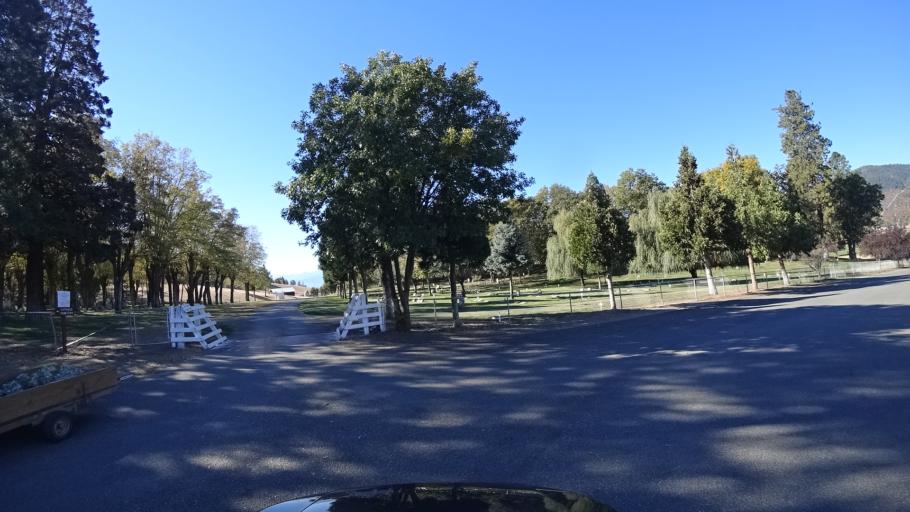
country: US
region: California
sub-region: Siskiyou County
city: Yreka
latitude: 41.5898
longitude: -122.8344
